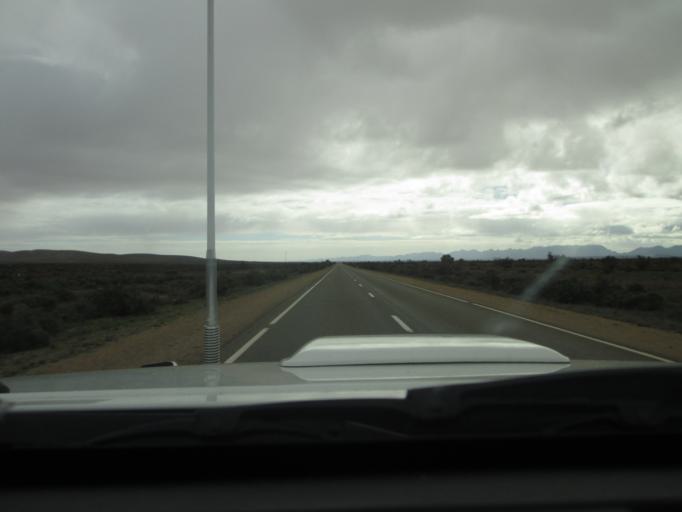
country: AU
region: South Australia
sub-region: Flinders Ranges
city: Quorn
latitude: -31.5176
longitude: 138.4274
